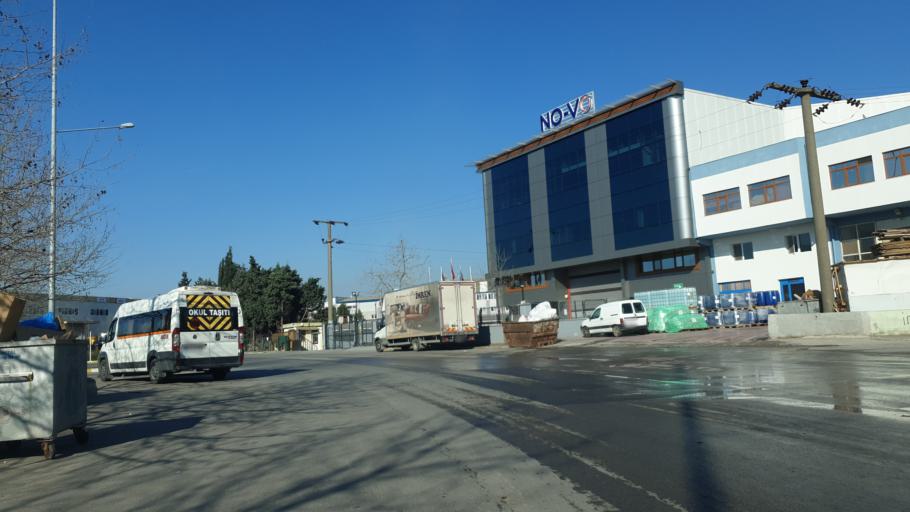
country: TR
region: Kocaeli
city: Balcik
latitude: 40.8776
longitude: 29.3668
